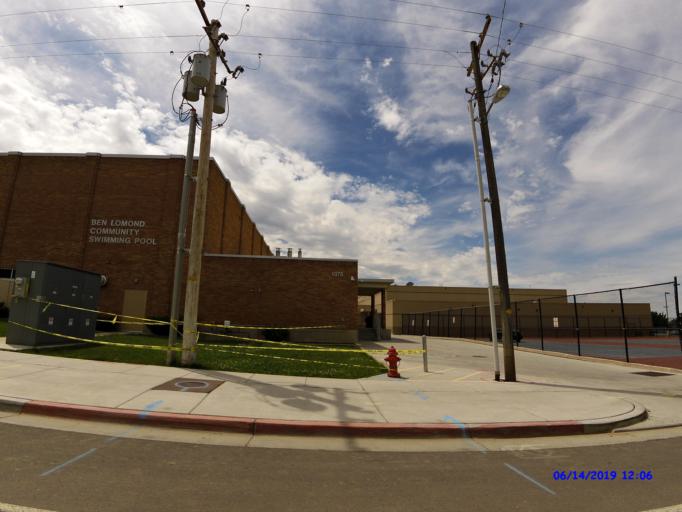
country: US
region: Utah
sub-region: Weber County
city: Ogden
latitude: 41.2515
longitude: -111.9512
